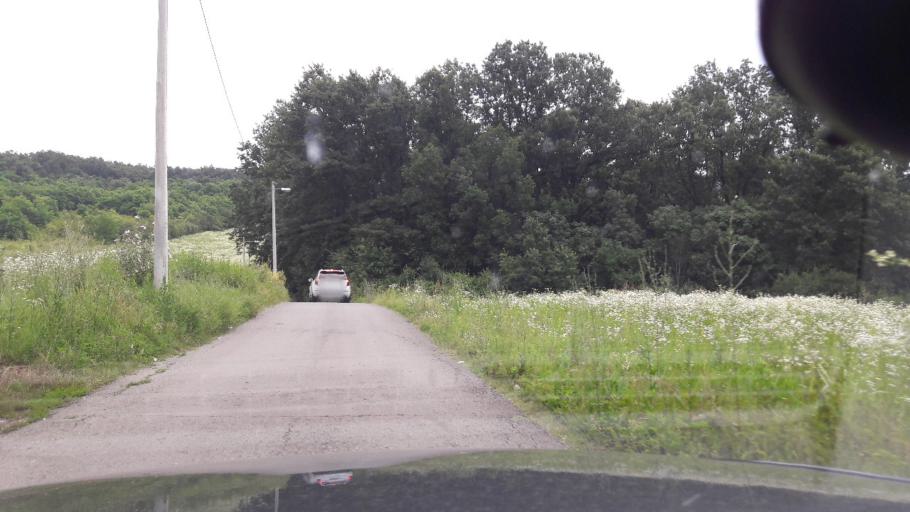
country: RS
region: Central Serbia
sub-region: Belgrade
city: Sopot
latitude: 44.6371
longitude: 20.5935
